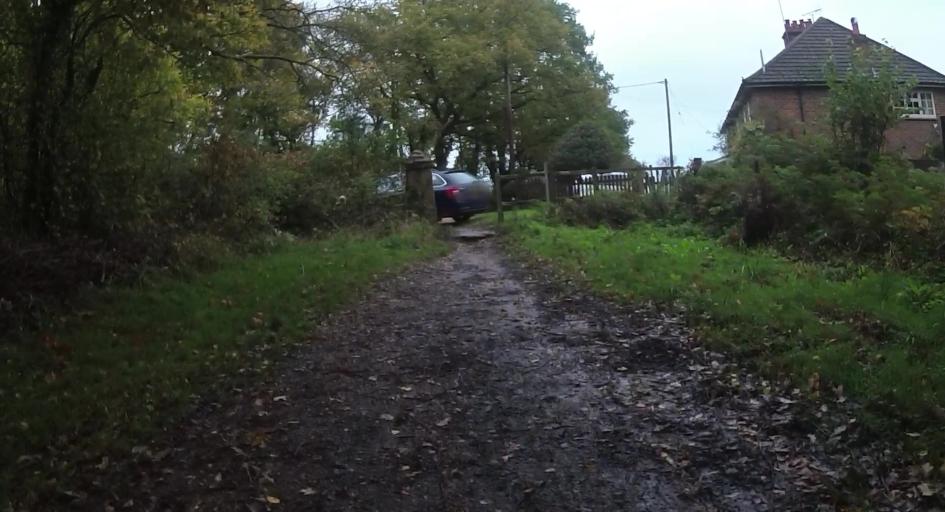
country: GB
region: England
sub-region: Surrey
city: Farnham
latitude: 51.2252
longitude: -0.8177
